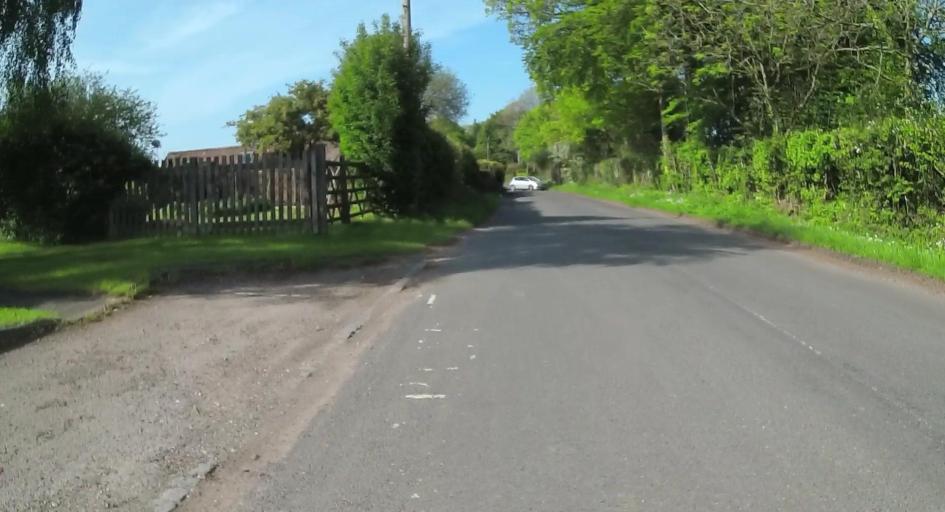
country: GB
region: England
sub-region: Hampshire
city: Four Marks
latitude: 51.1520
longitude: -1.0561
